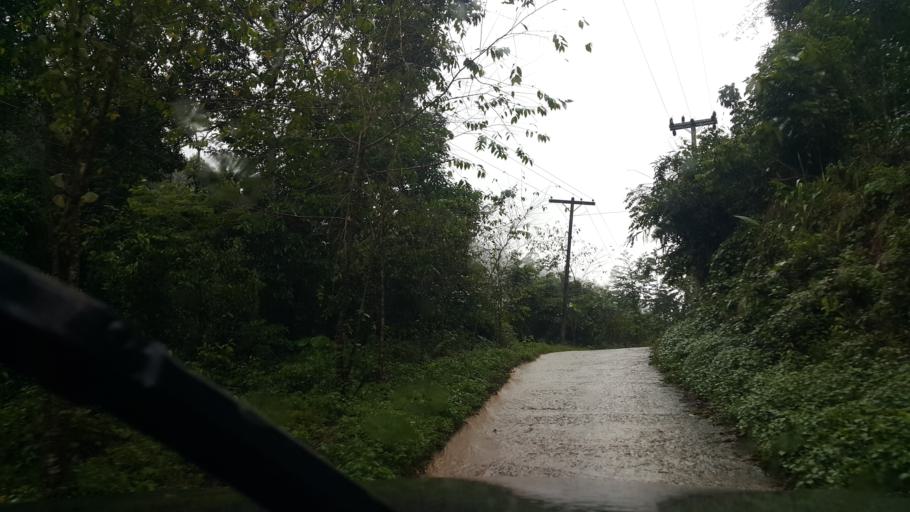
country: TH
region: Chiang Rai
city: Wiang Pa Pao
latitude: 19.1326
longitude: 99.3530
